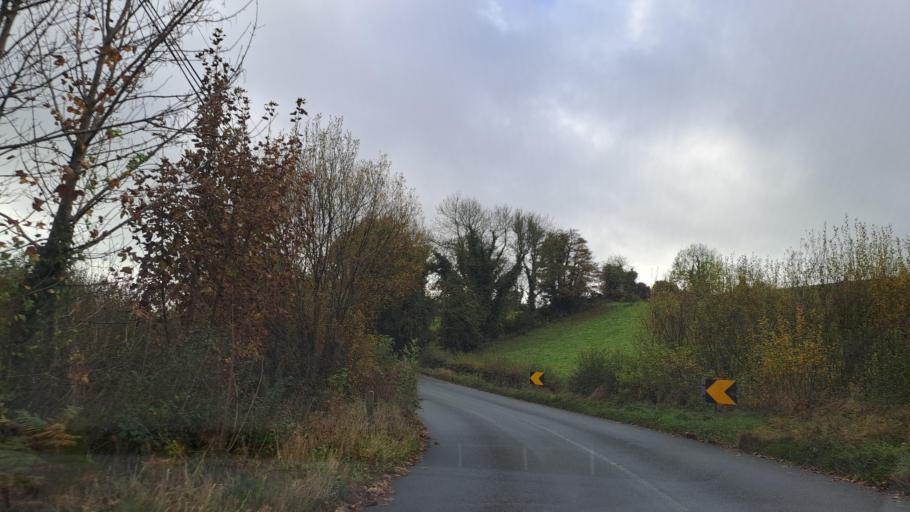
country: IE
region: Ulster
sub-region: An Cabhan
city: Virginia
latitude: 53.8567
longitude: -7.0463
